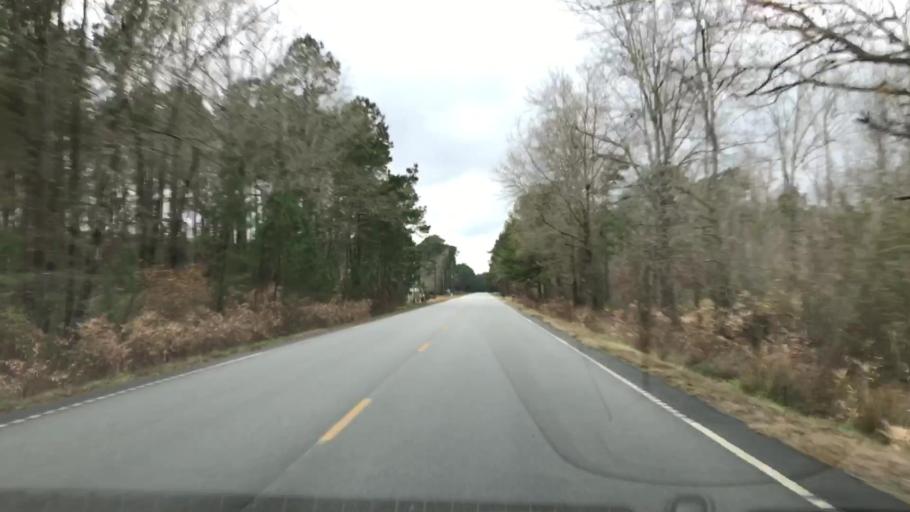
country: US
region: South Carolina
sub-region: Berkeley County
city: Saint Stephen
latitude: 33.2881
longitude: -79.7631
